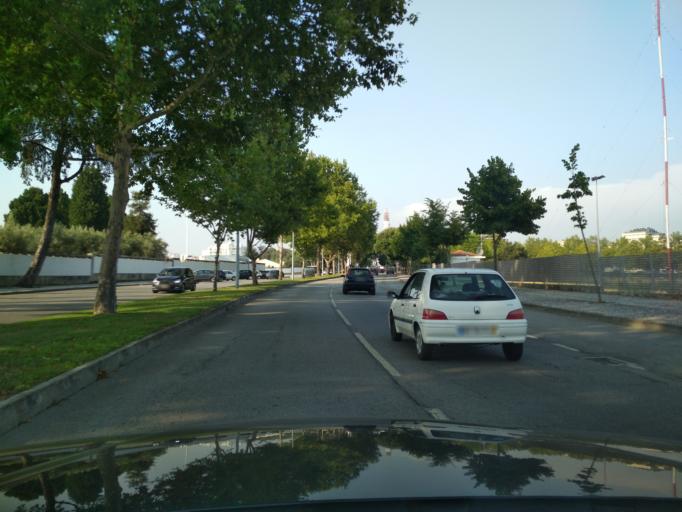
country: PT
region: Viseu
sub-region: Viseu
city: Viseu
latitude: 40.6456
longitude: -7.9228
